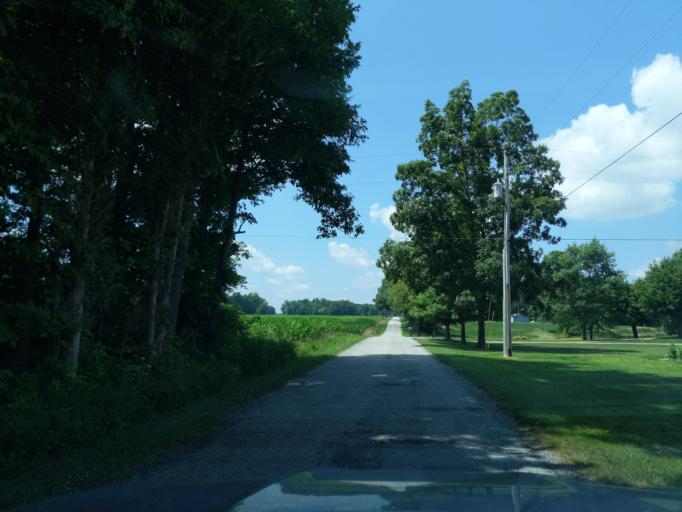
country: US
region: Indiana
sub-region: Ripley County
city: Osgood
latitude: 39.2191
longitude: -85.3935
